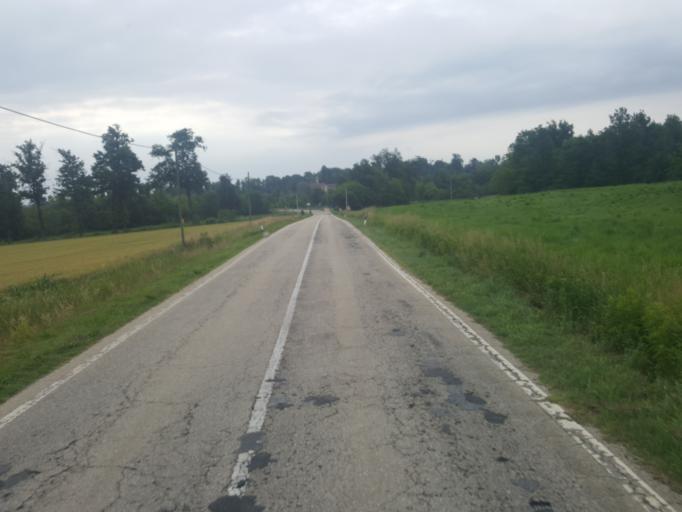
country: IT
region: Piedmont
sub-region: Provincia di Cuneo
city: Ceresole Alba
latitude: 44.8509
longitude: 7.8399
